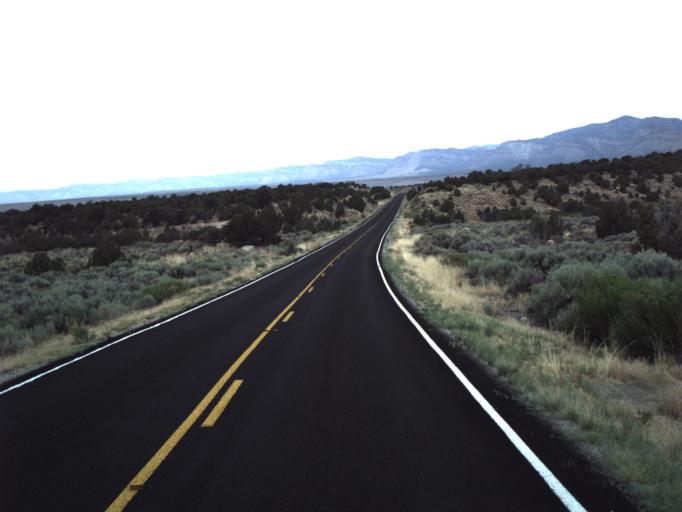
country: US
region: Utah
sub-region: Carbon County
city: East Carbon City
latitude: 39.4687
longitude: -110.3961
